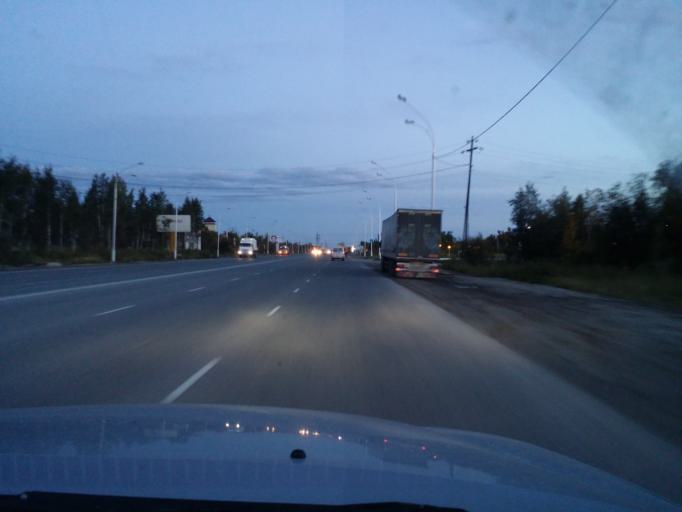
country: RU
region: Khanty-Mansiyskiy Avtonomnyy Okrug
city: Nizhnevartovsk
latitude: 60.9641
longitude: 76.5303
